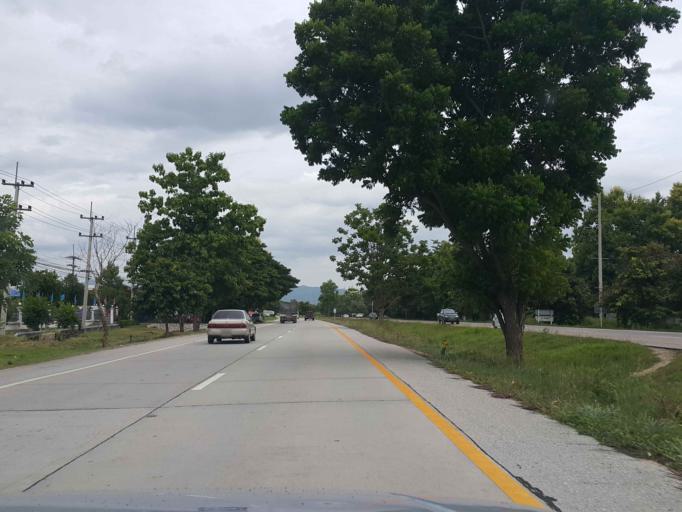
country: TH
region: Lampang
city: Lampang
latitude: 18.2949
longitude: 99.4180
